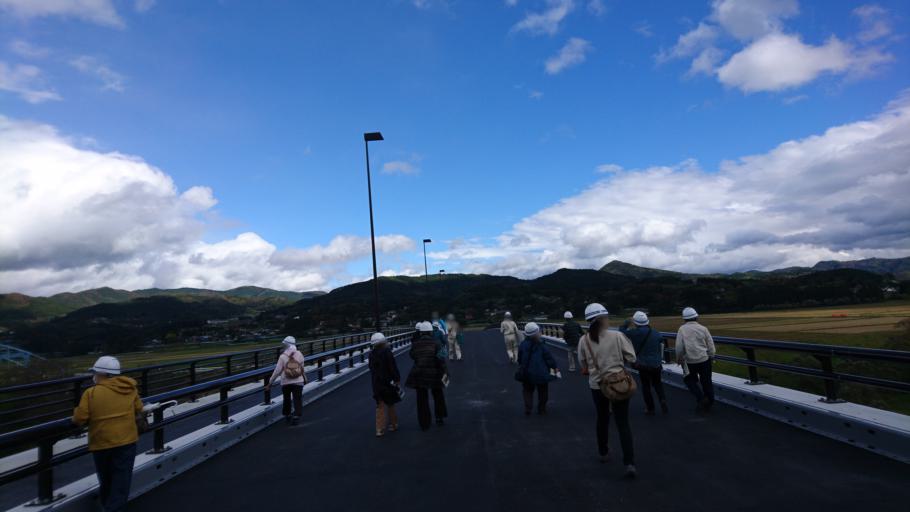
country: JP
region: Iwate
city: Ichinoseki
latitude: 38.9547
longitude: 141.1593
